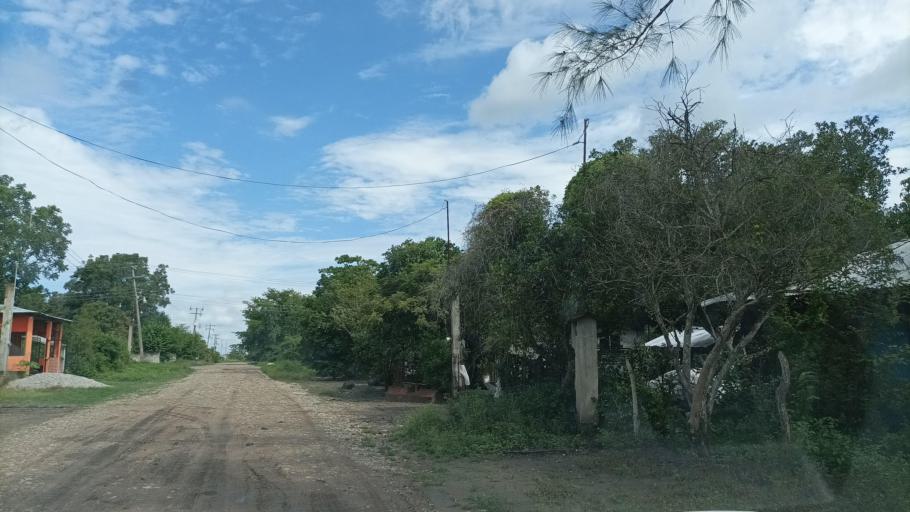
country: MX
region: Veracruz
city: Panuco
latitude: 21.9443
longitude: -98.1377
